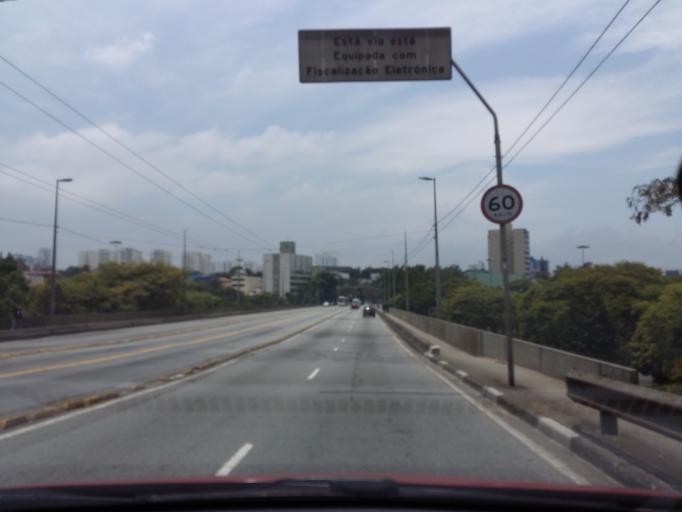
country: BR
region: Sao Paulo
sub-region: Sao Bernardo Do Campo
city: Sao Bernardo do Campo
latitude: -23.6899
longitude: -46.5618
